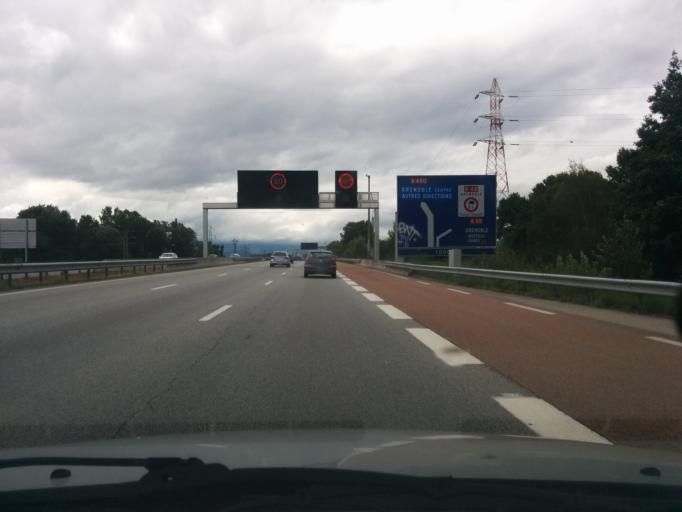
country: FR
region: Rhone-Alpes
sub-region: Departement de l'Isere
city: Saint-Egreve
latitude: 45.2266
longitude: 5.6683
